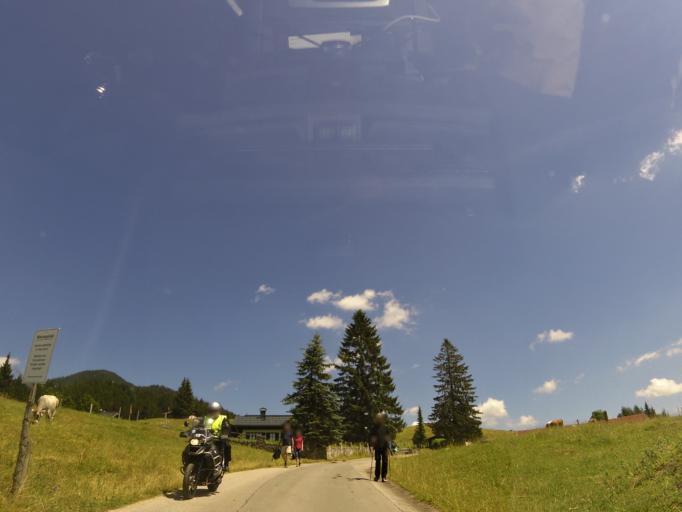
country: AT
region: Tyrol
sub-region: Politischer Bezirk Kitzbuhel
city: Waidring
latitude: 47.6579
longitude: 12.5800
